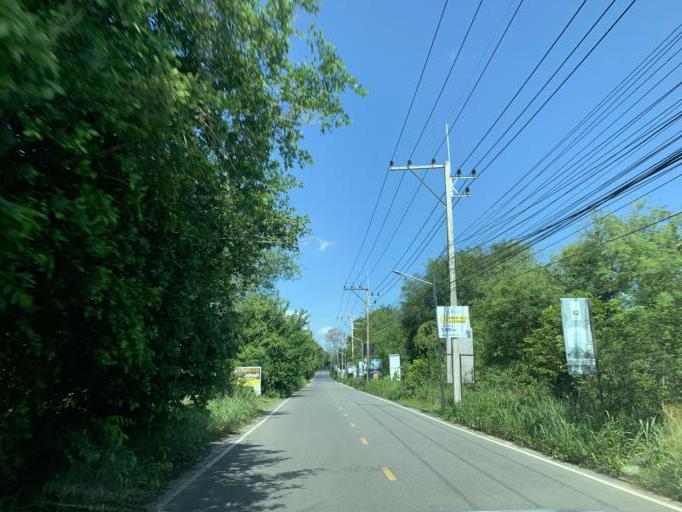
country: TH
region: Chon Buri
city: Sattahip
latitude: 12.7751
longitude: 100.9053
